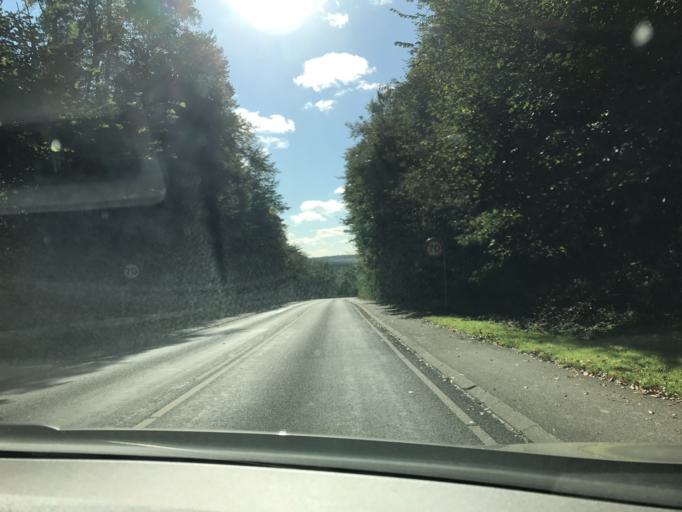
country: DK
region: South Denmark
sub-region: Assens Kommune
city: Vissenbjerg
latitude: 55.3838
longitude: 10.1325
